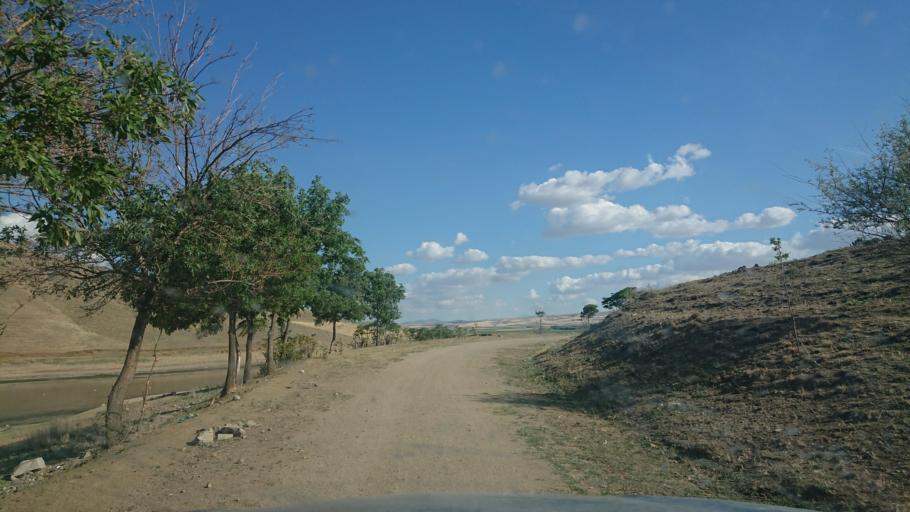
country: TR
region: Aksaray
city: Sariyahsi
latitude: 39.0207
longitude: 33.8965
